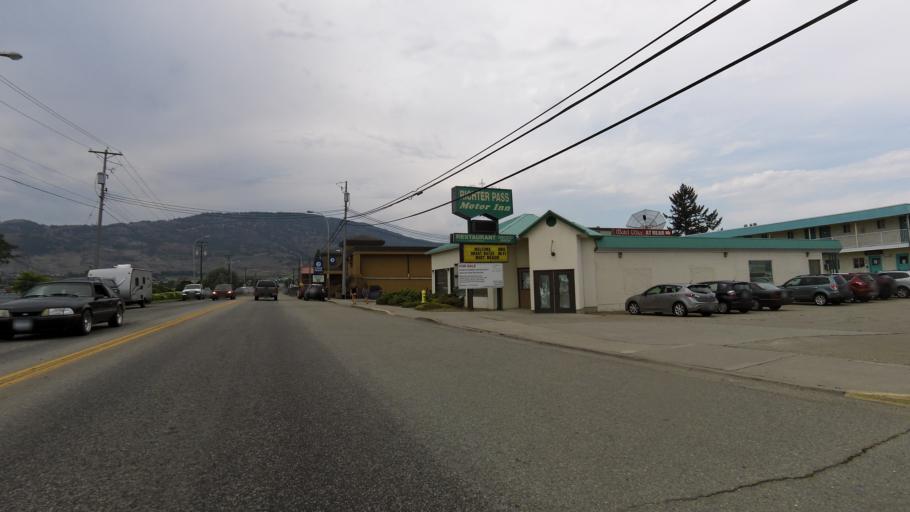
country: CA
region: British Columbia
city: Osoyoos
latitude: 49.0284
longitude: -119.4545
